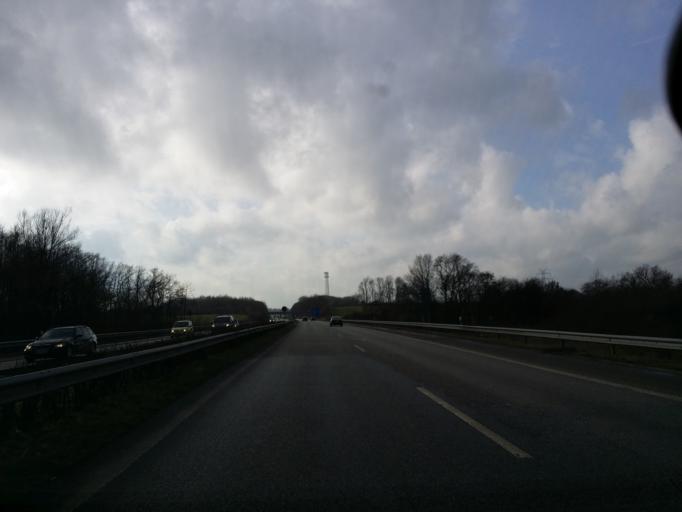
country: DE
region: Schleswig-Holstein
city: Achterwehr
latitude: 54.3200
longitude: 9.9608
